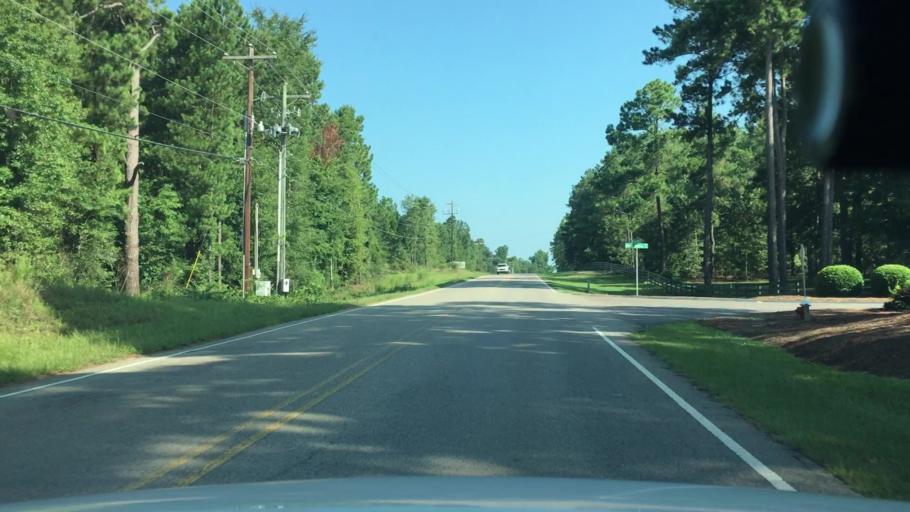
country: US
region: South Carolina
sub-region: Aiken County
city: Graniteville
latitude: 33.5980
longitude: -81.8399
